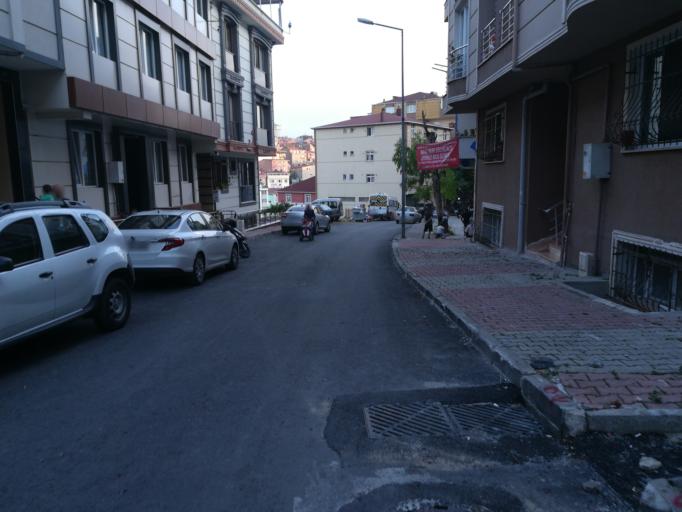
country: TR
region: Istanbul
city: Sisli
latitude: 41.0964
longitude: 28.9909
